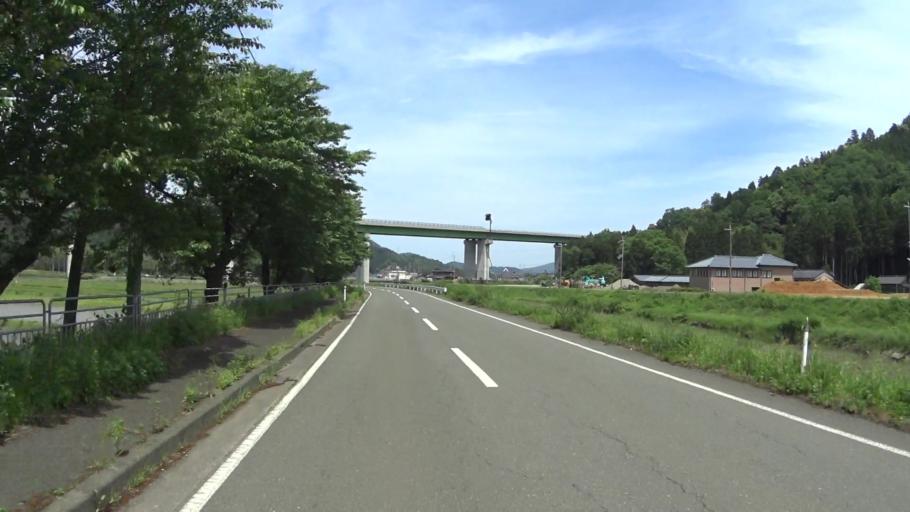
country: JP
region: Fukui
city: Obama
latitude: 35.4469
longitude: 135.5539
